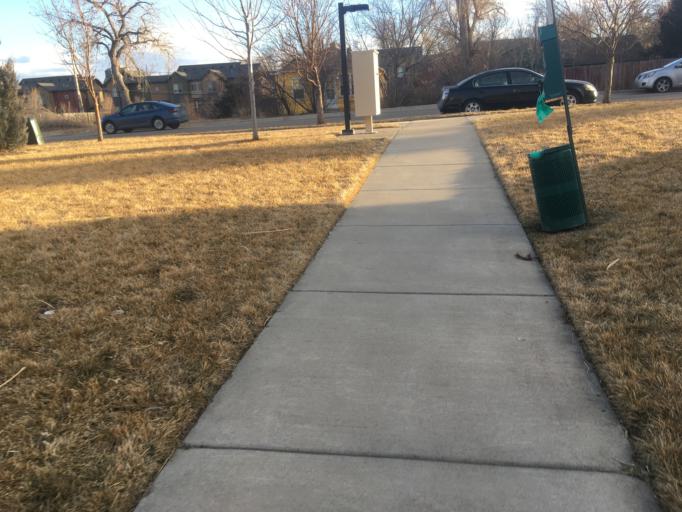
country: US
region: Colorado
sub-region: Boulder County
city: Lafayette
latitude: 40.0014
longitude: -105.0813
